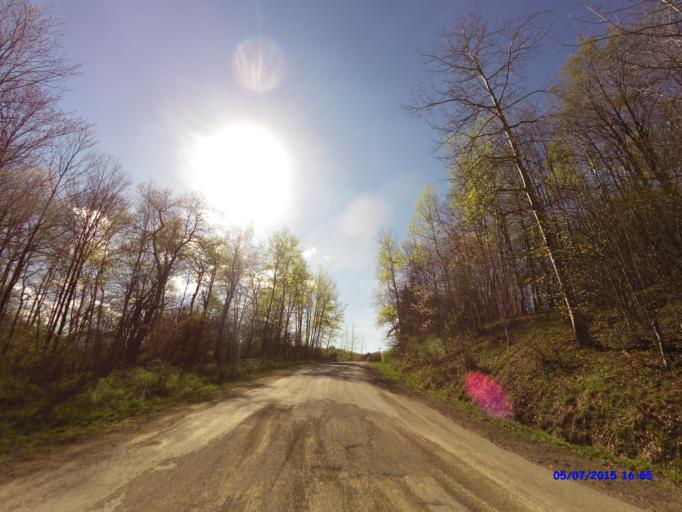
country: US
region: New York
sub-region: Cattaraugus County
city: Little Valley
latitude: 42.3020
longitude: -78.7563
